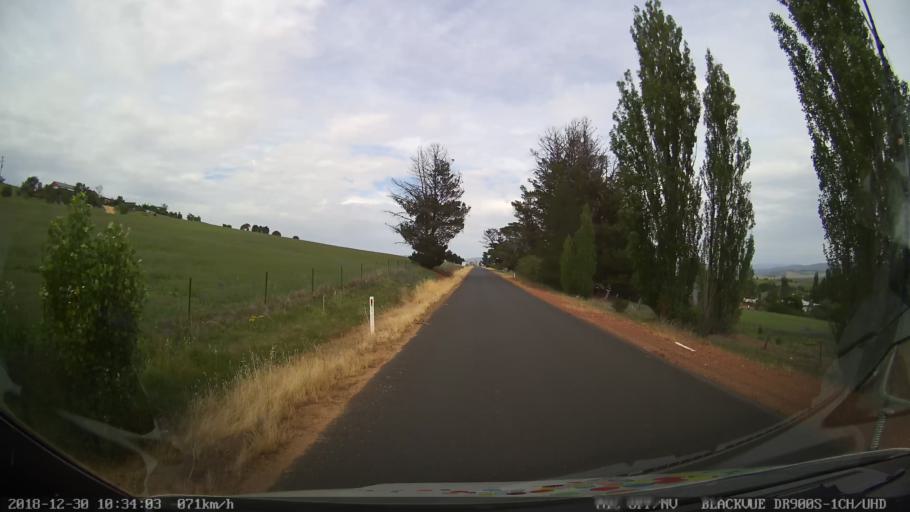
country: AU
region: New South Wales
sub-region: Snowy River
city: Berridale
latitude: -36.4994
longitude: 148.8450
